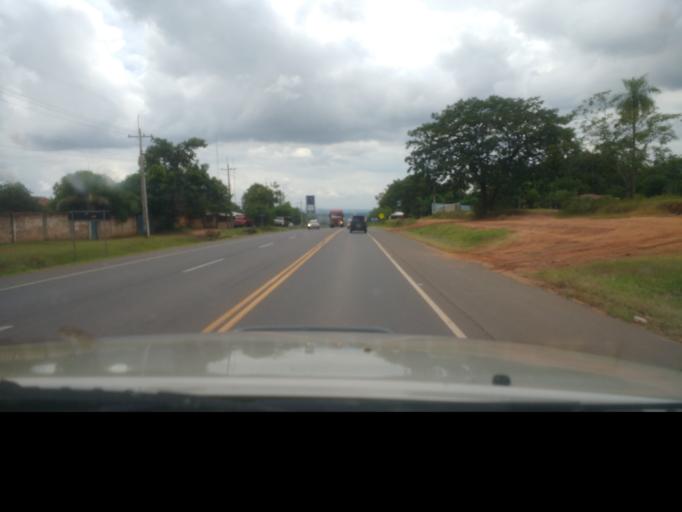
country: PY
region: Cordillera
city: Arroyos y Esteros
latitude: -25.0587
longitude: -57.1502
